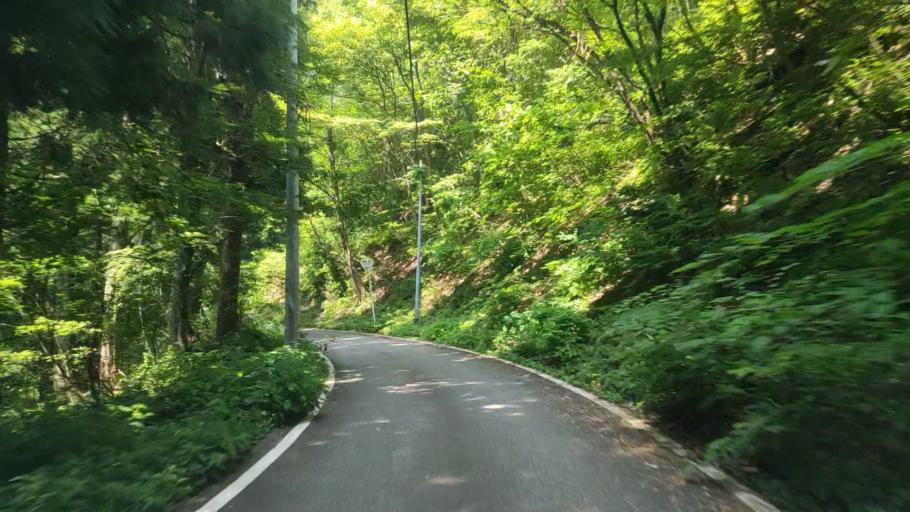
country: JP
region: Fukui
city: Katsuyama
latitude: 36.2386
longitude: 136.5293
